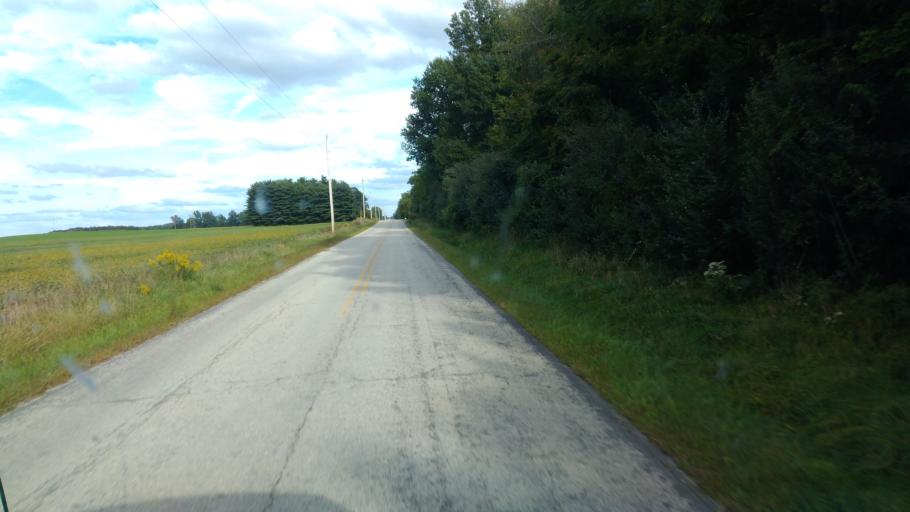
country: US
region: Ohio
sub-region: Crawford County
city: Bucyrus
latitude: 40.9212
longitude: -82.9945
